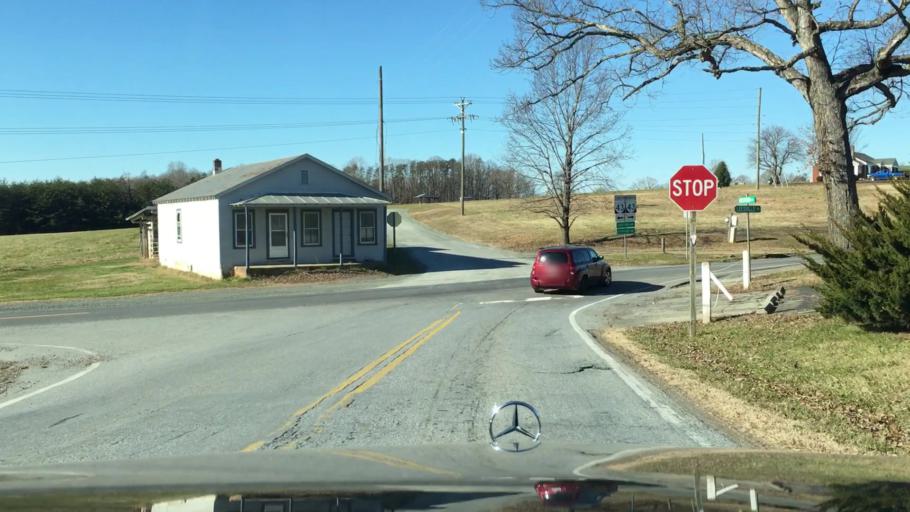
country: US
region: Virginia
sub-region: Pittsylvania County
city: Motley
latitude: 37.1928
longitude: -79.4270
